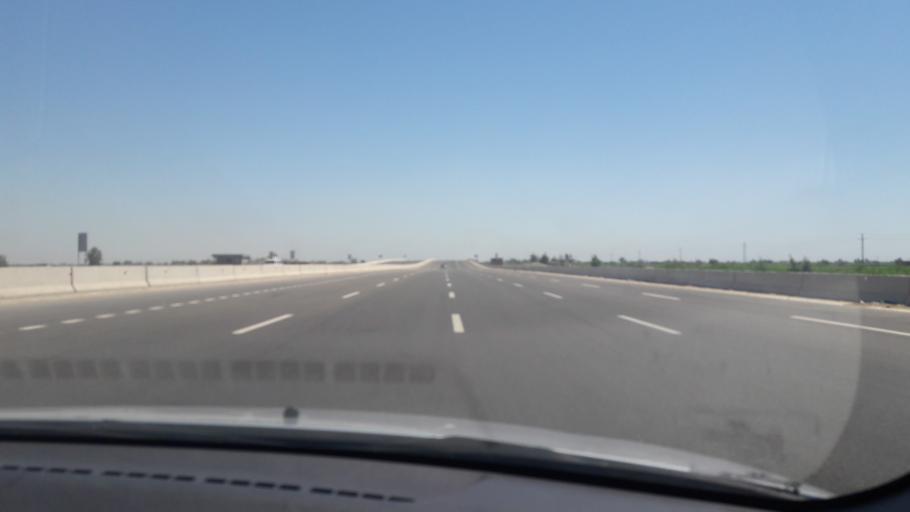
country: EG
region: Muhafazat Bur Sa`id
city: Port Said
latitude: 31.1786
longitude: 32.2354
